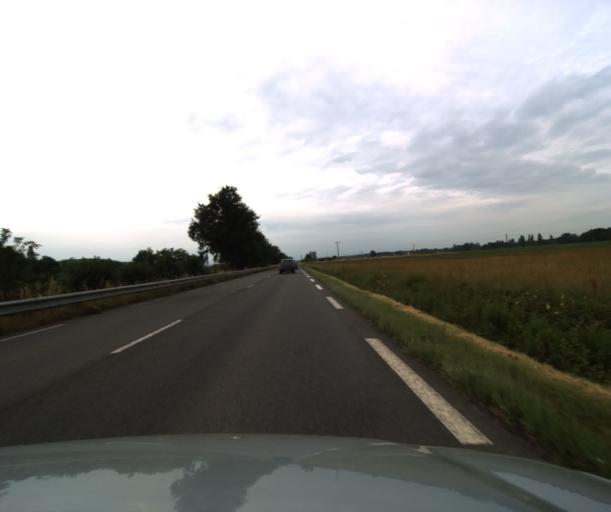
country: FR
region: Midi-Pyrenees
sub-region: Departement des Hautes-Pyrenees
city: Rabastens-de-Bigorre
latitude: 43.3618
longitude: 0.1410
